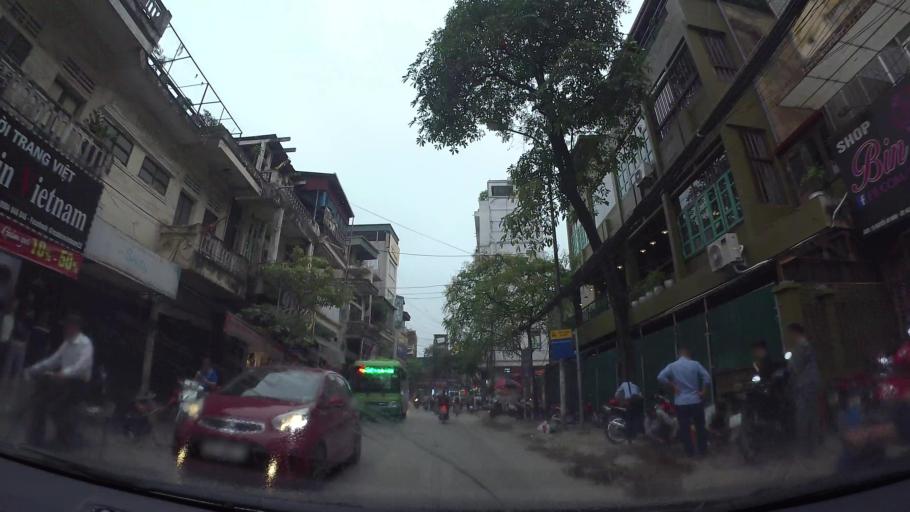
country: VN
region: Ha Noi
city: Hai BaTrung
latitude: 20.9888
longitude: 105.8464
